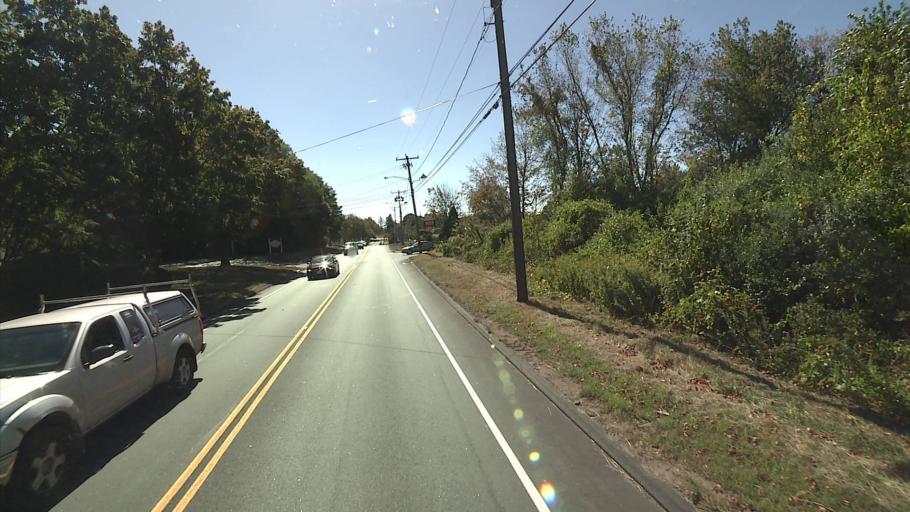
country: US
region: Connecticut
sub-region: New Haven County
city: Prospect
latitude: 41.5061
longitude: -72.9802
